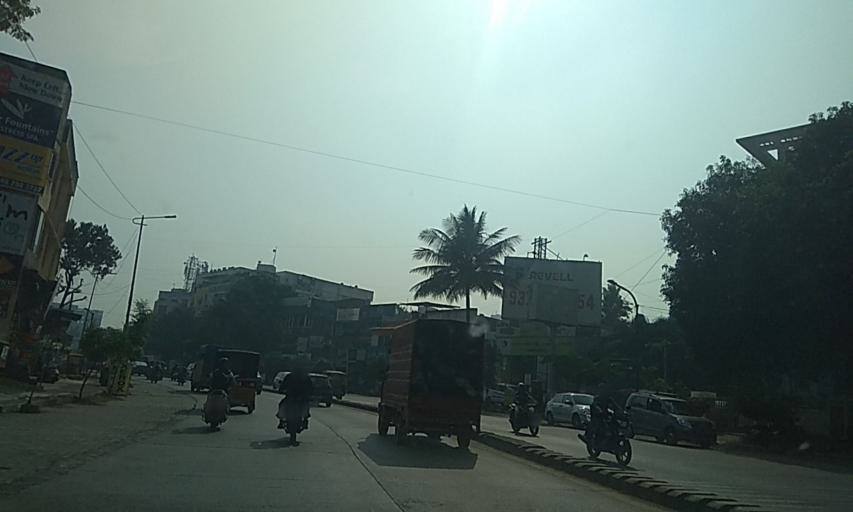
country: IN
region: Maharashtra
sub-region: Pune Division
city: Pimpri
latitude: 18.5620
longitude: 73.7843
